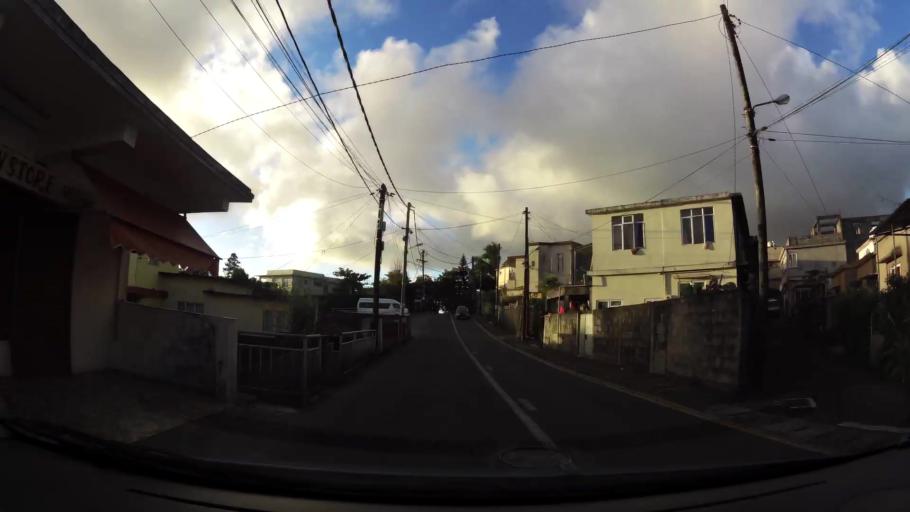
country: MU
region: Plaines Wilhems
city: Curepipe
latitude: -20.3108
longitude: 57.5297
